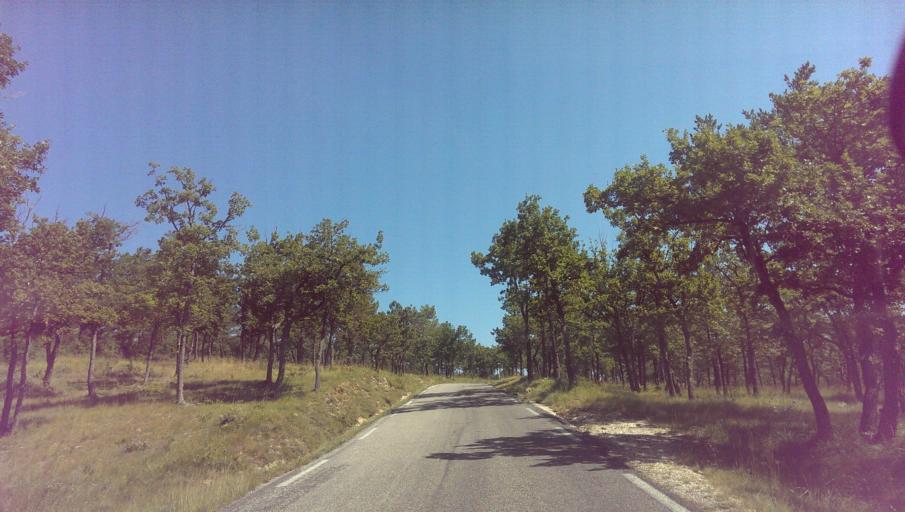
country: FR
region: Provence-Alpes-Cote d'Azur
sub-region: Departement du Vaucluse
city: Gordes
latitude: 43.9541
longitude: 5.2054
